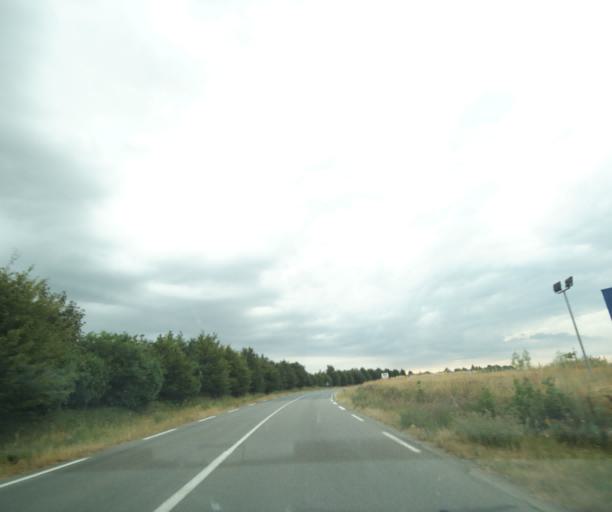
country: FR
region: Pays de la Loire
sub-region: Departement de la Vendee
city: Lucon
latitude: 46.4597
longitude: -1.1477
